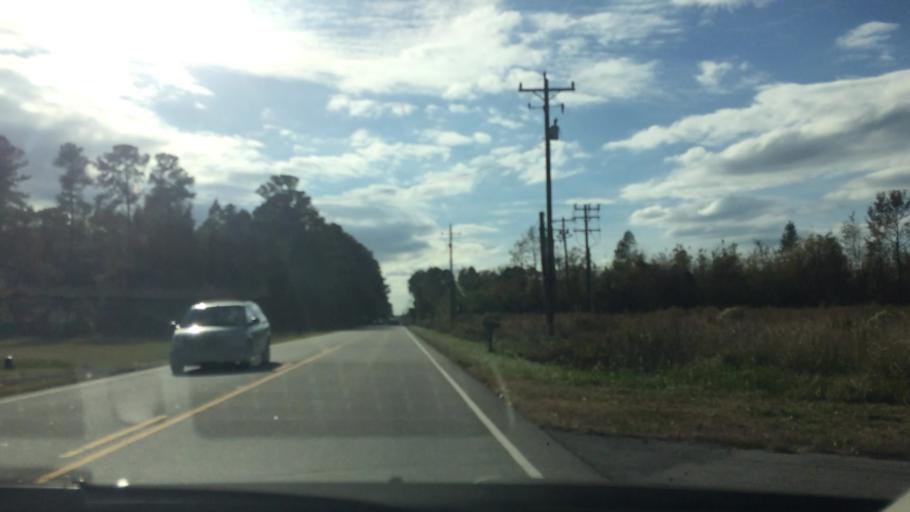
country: US
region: North Carolina
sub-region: Wayne County
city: Elroy
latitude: 35.4361
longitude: -77.8633
